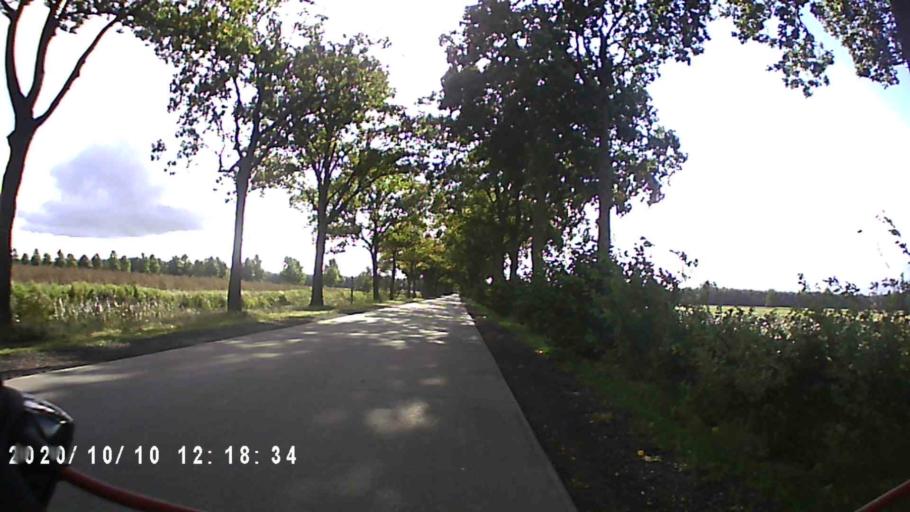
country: NL
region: Friesland
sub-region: Gemeente Heerenveen
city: Jubbega
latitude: 53.0156
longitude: 6.1744
